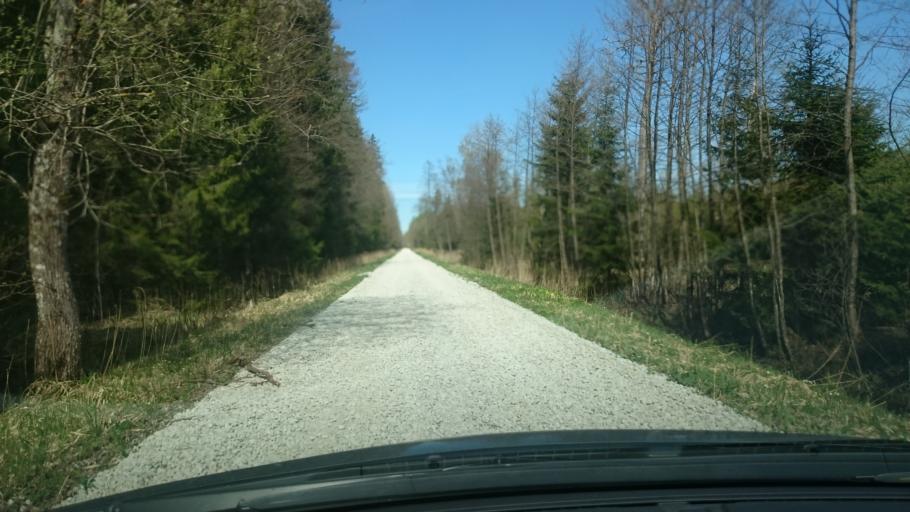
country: EE
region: Ida-Virumaa
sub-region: Sillamaee linn
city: Sillamae
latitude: 59.1638
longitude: 27.7997
